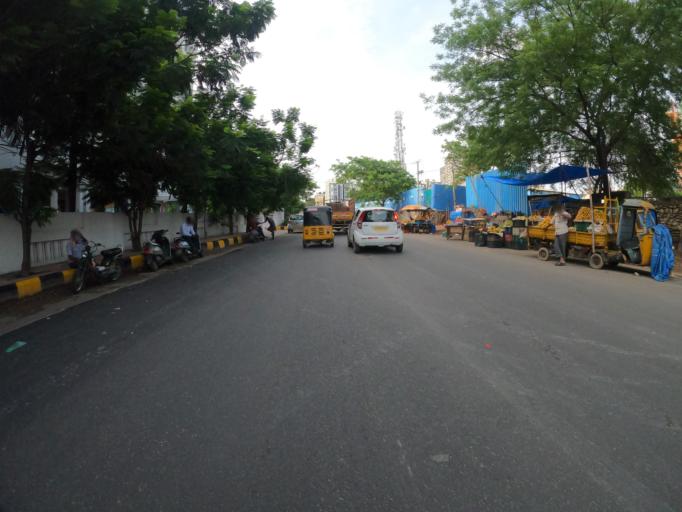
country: IN
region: Telangana
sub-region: Hyderabad
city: Hyderabad
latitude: 17.4097
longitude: 78.3948
